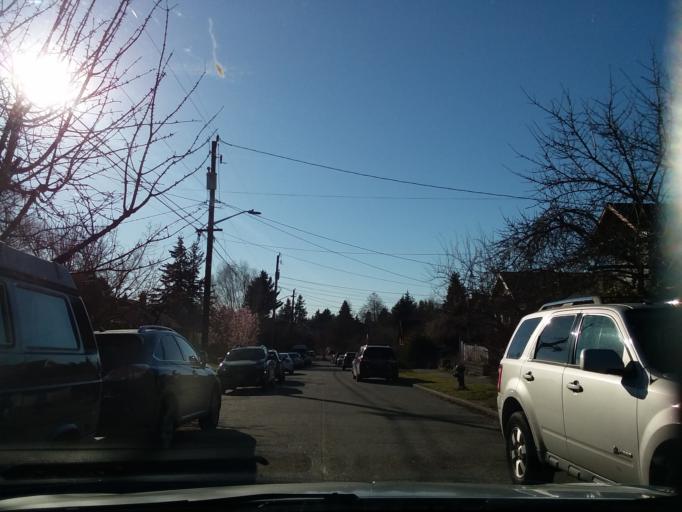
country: US
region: Washington
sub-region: King County
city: Shoreline
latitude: 47.6826
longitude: -122.3617
